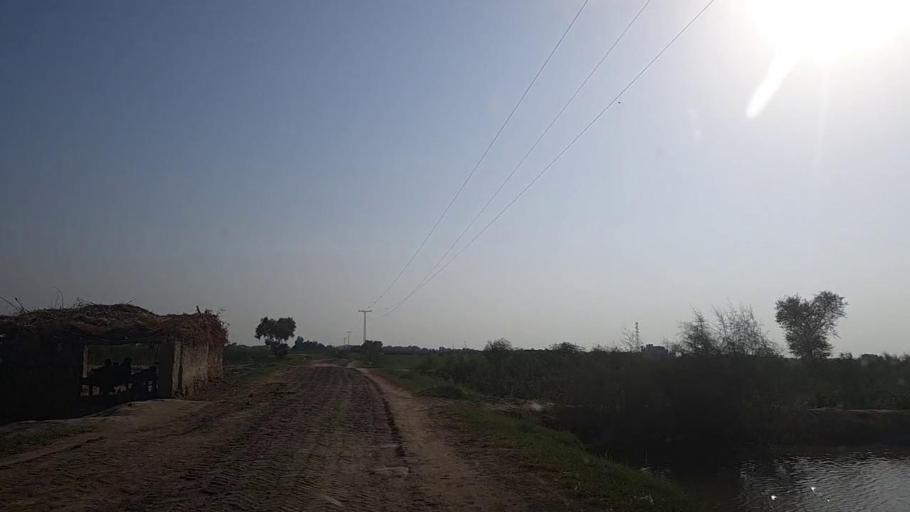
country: PK
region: Sindh
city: Khanpur
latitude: 27.7295
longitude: 69.3128
